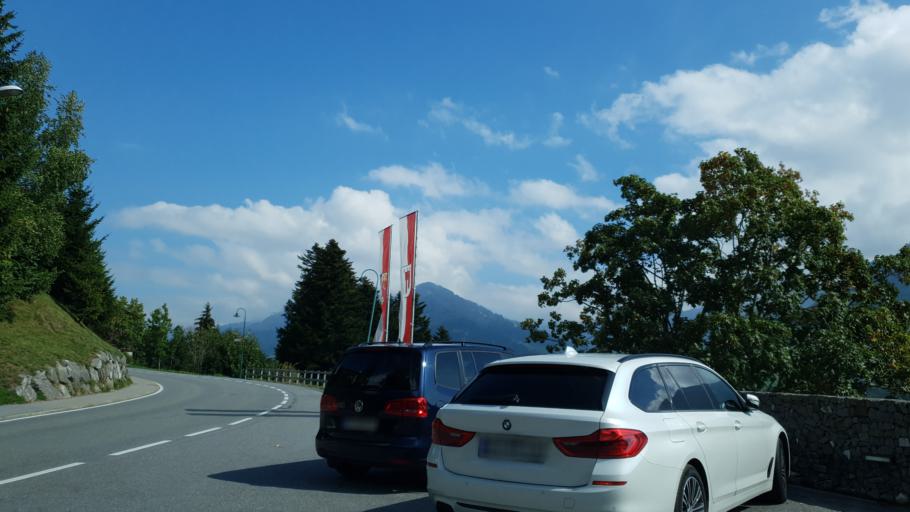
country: AT
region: Vorarlberg
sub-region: Politischer Bezirk Bludenz
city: Blons
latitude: 47.2205
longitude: 9.8153
